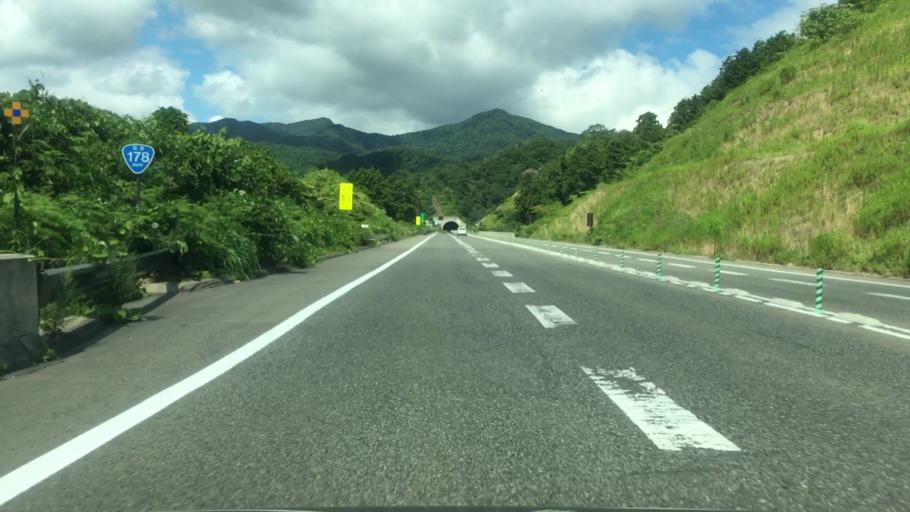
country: JP
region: Hyogo
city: Toyooka
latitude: 35.6292
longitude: 134.6179
